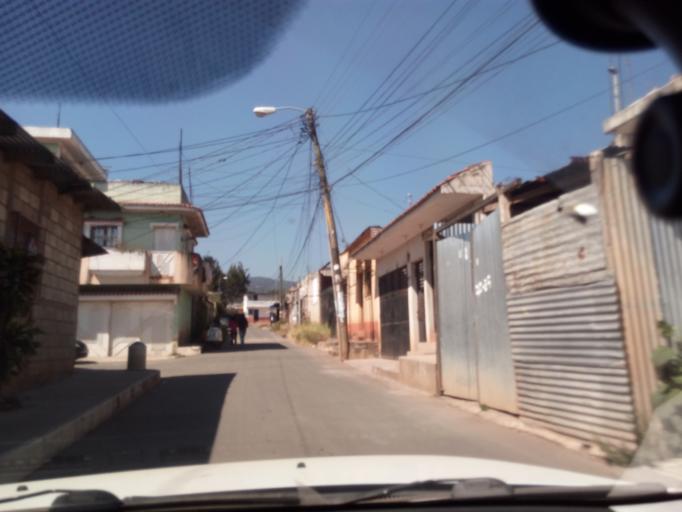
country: GT
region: Guatemala
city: Mixco
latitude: 14.6175
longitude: -90.5861
